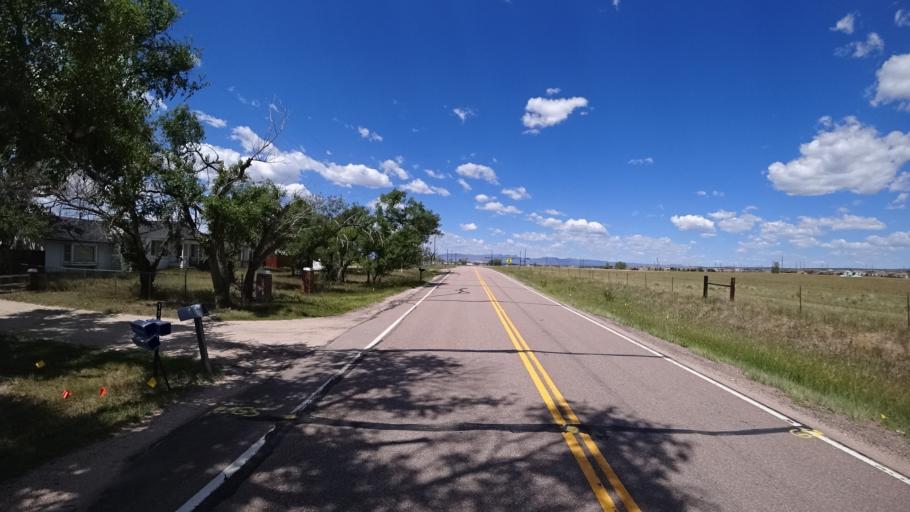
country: US
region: Colorado
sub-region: El Paso County
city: Cimarron Hills
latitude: 38.9263
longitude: -104.6145
